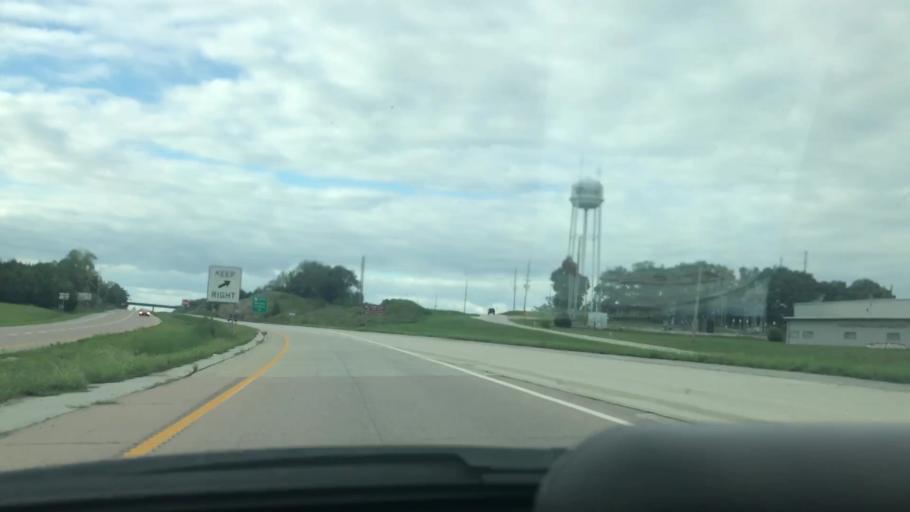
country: US
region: Missouri
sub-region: Benton County
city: Warsaw
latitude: 38.2465
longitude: -93.3605
